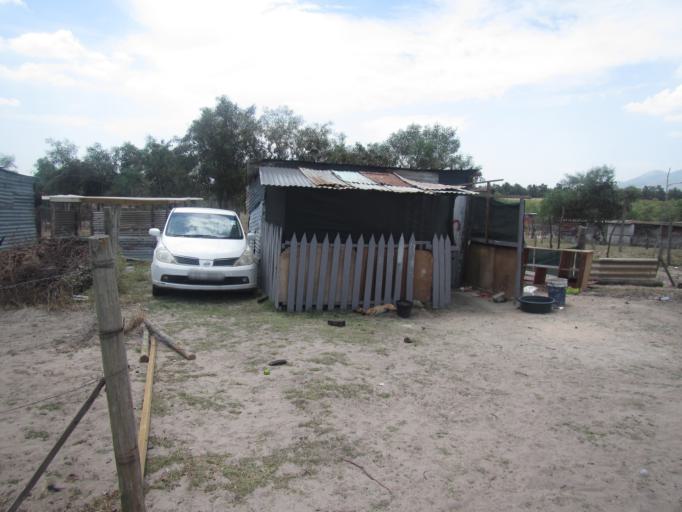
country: ZA
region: Western Cape
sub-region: Cape Winelands District Municipality
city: Stellenbosch
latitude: -33.8044
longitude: 18.8563
